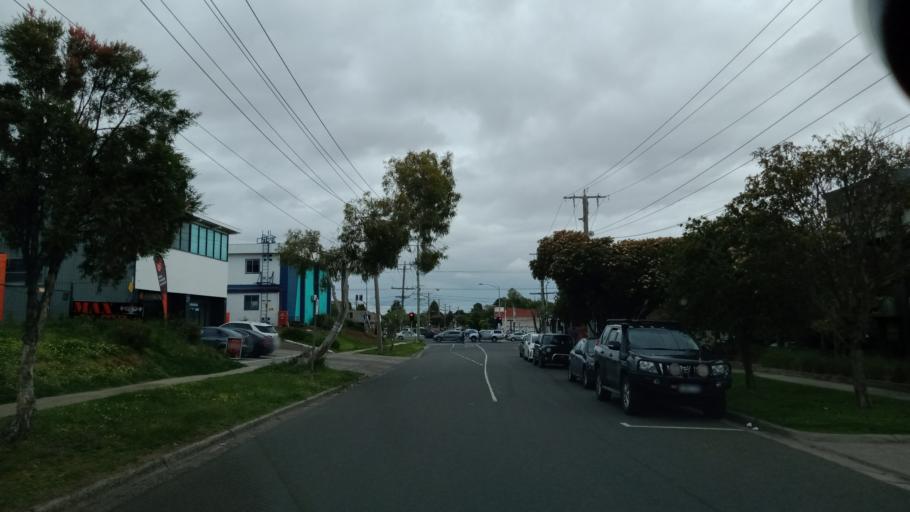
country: AU
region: Victoria
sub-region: Monash
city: Notting Hill
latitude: -37.8873
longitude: 145.1578
